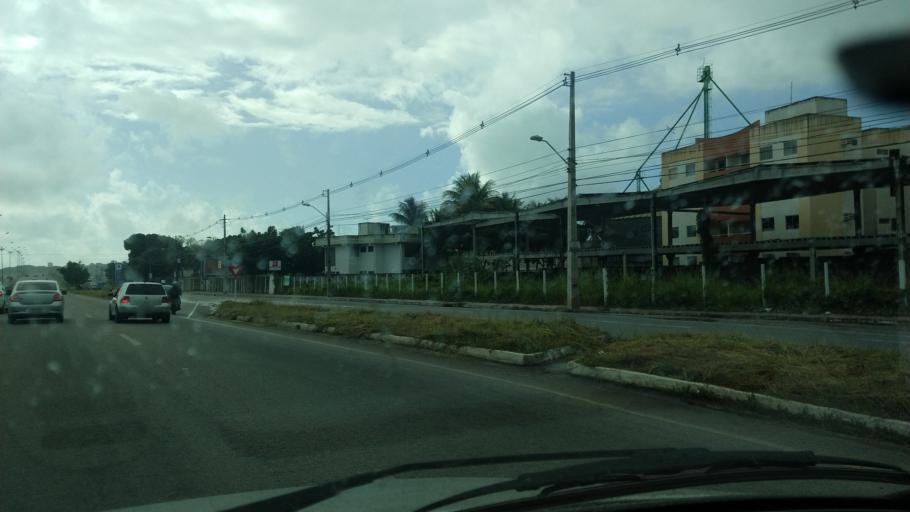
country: BR
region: Rio Grande do Norte
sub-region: Parnamirim
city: Parnamirim
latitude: -5.8878
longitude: -35.2363
